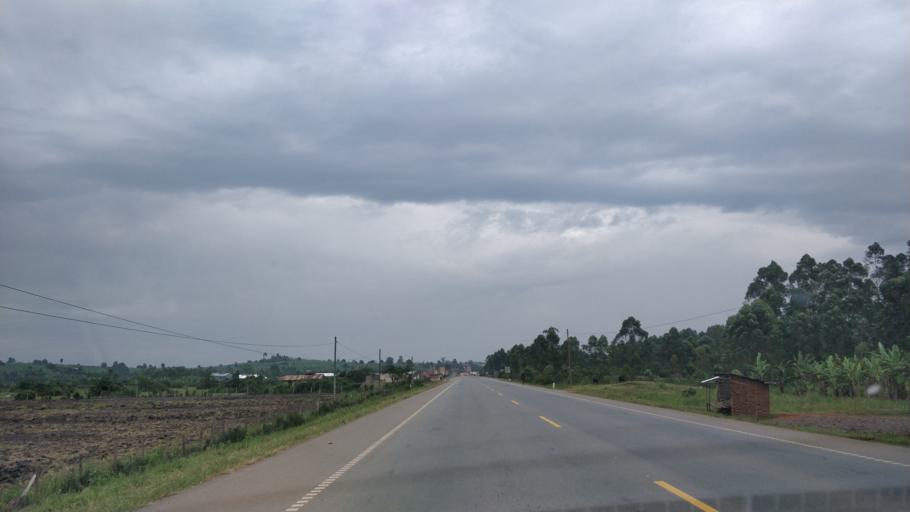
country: UG
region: Western Region
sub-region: Sheema District
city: Kibingo
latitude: -0.6652
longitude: 30.4487
